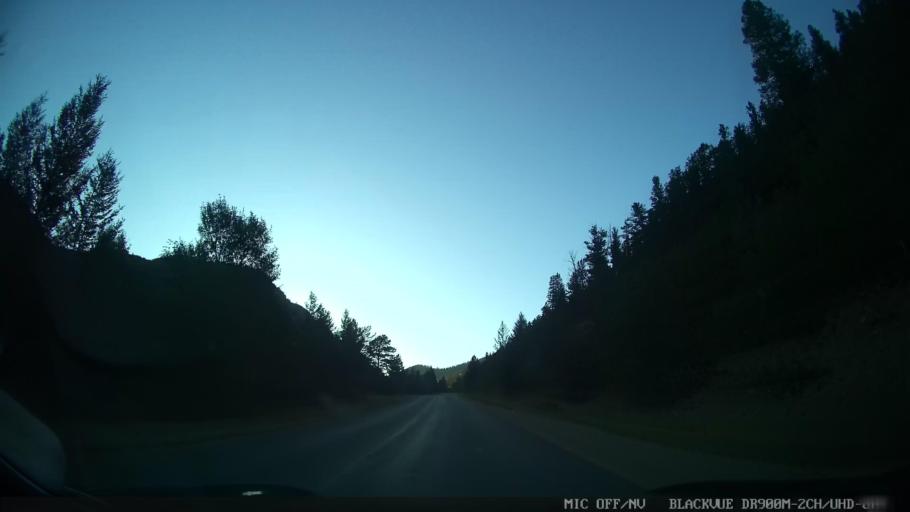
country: US
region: Colorado
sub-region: Grand County
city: Kremmling
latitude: 39.9991
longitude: -106.4824
